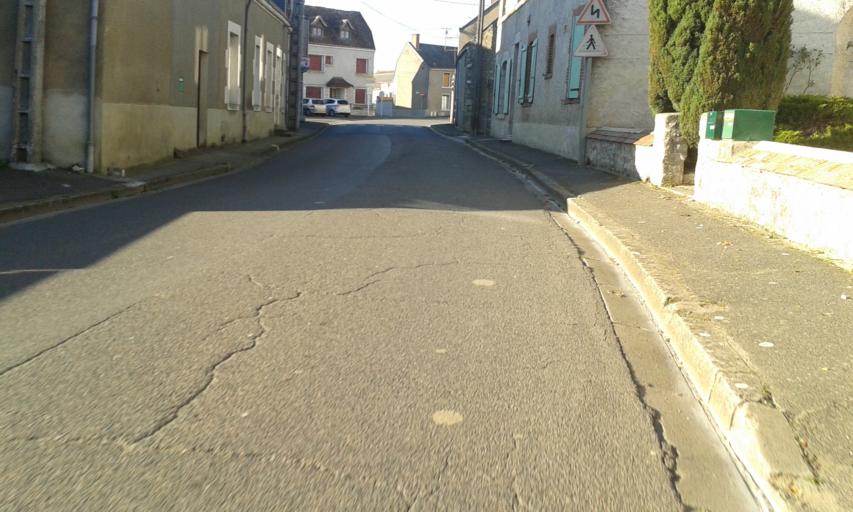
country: FR
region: Centre
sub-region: Departement du Loir-et-Cher
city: Oucques
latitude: 47.8308
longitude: 1.3817
